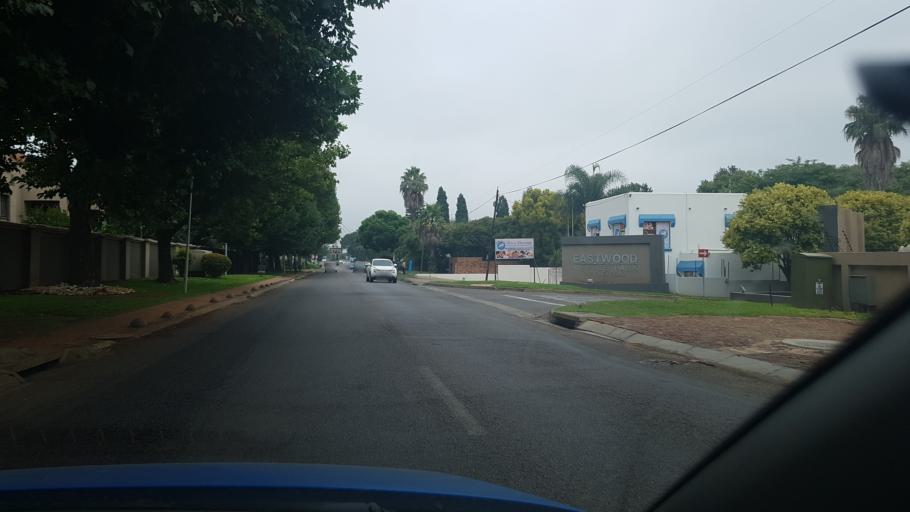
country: ZA
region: Gauteng
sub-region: Ekurhuleni Metropolitan Municipality
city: Germiston
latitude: -26.1666
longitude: 28.1500
